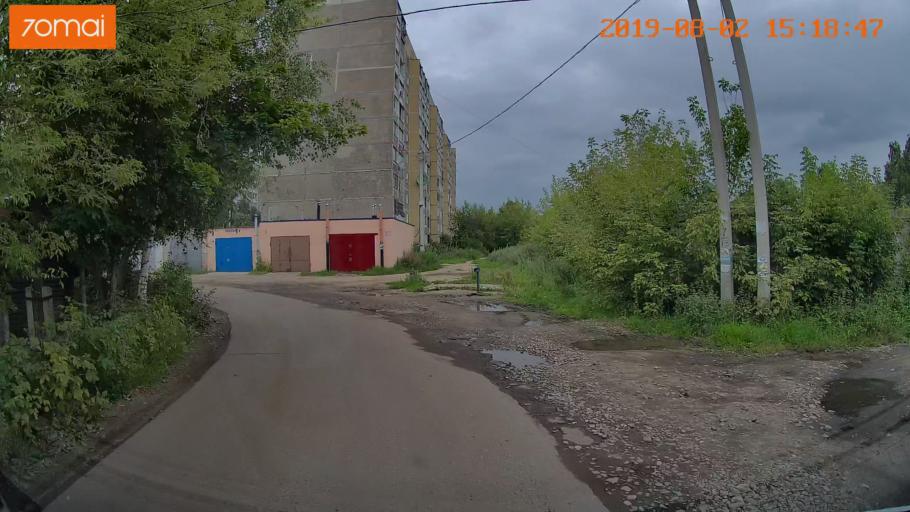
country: RU
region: Ivanovo
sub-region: Gorod Ivanovo
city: Ivanovo
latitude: 56.9799
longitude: 40.9728
